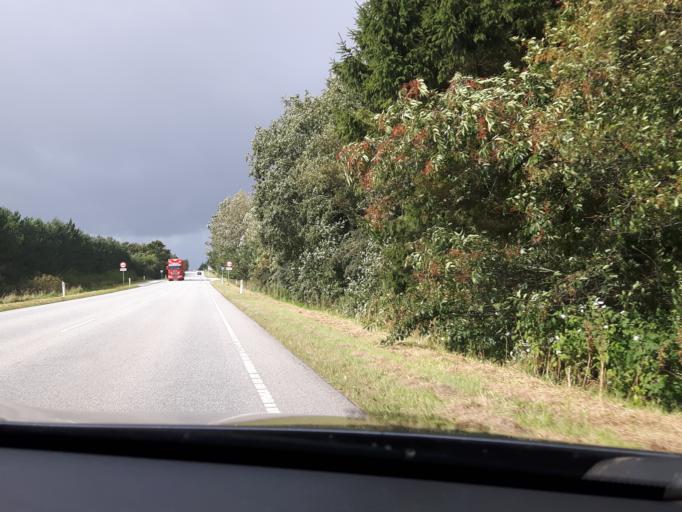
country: DK
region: North Denmark
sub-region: Jammerbugt Kommune
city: Fjerritslev
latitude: 57.0883
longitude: 9.3519
